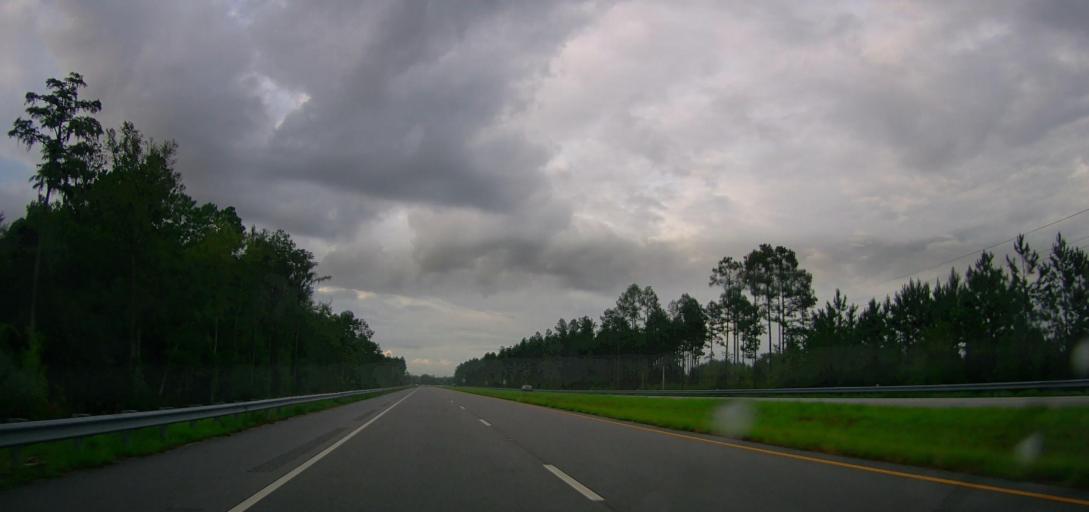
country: US
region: Georgia
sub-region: Ware County
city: Deenwood
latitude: 31.1684
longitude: -82.4121
